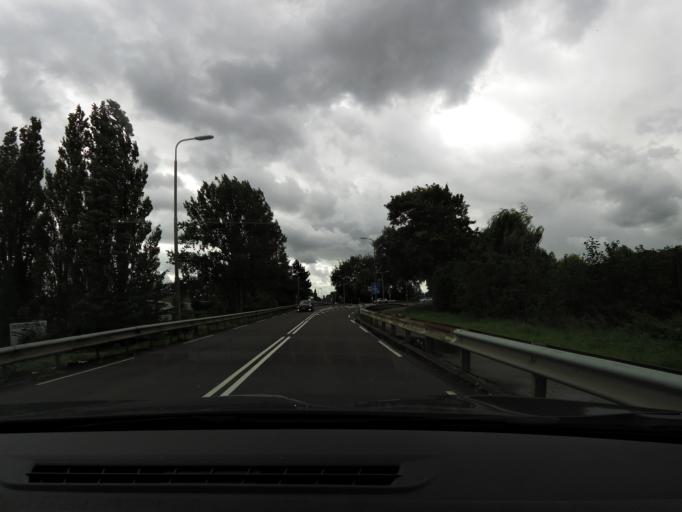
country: NL
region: South Holland
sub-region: Gemeente Oud-Beijerland
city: Oud-Beijerland
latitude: 51.8214
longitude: 4.4415
